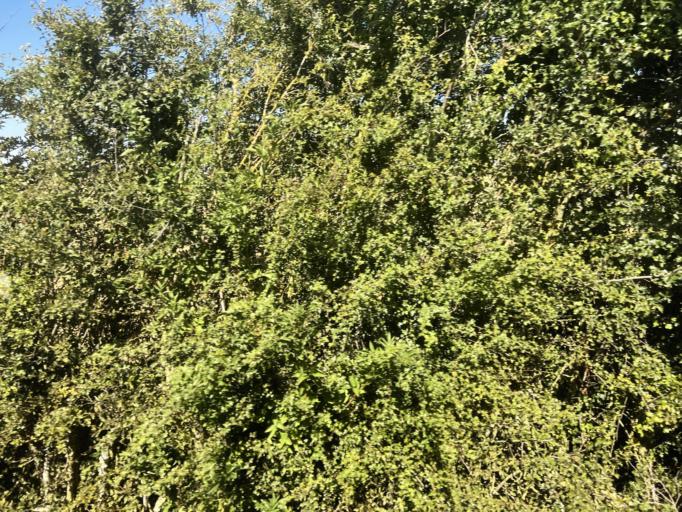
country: GB
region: England
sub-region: Lincolnshire
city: Spilsby
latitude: 53.0724
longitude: 0.0745
